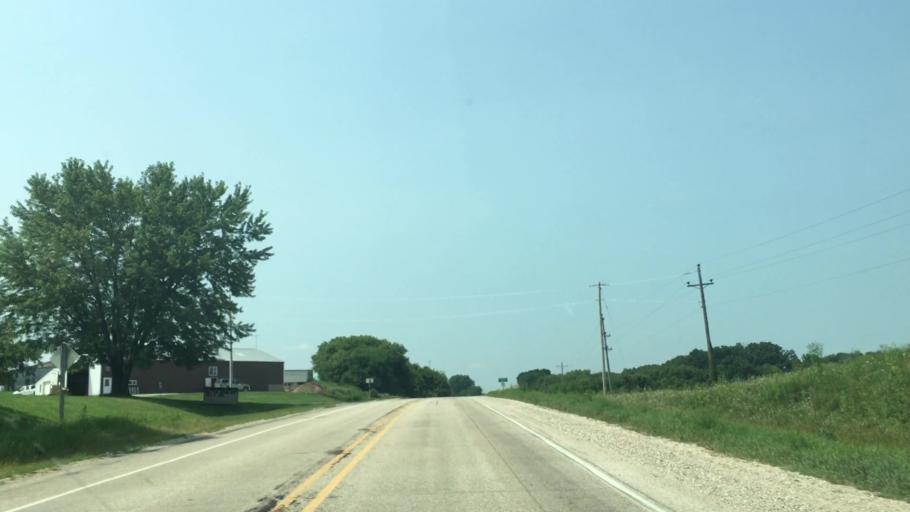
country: US
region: Iowa
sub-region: Fayette County
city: West Union
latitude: 43.0813
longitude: -91.8435
